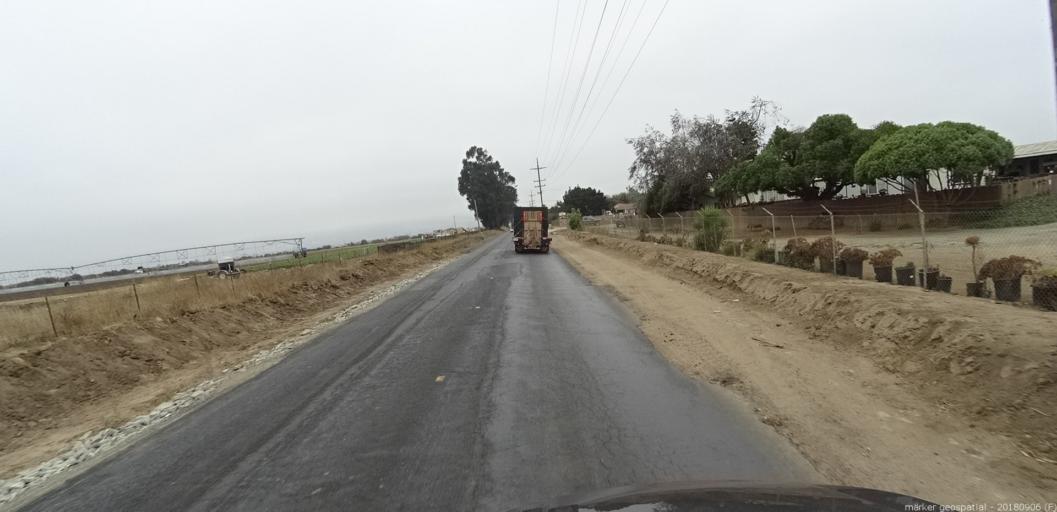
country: US
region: California
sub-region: Monterey County
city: Chualar
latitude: 36.6256
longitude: -121.5470
